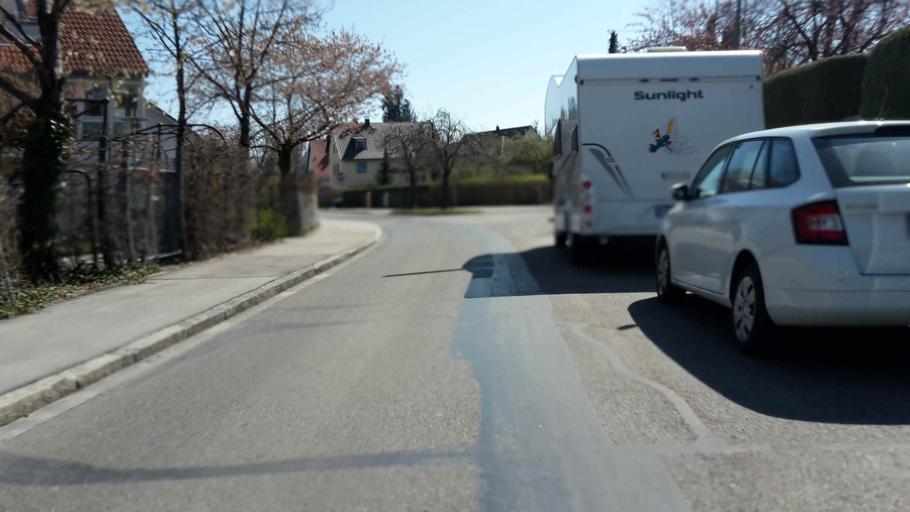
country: DE
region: Bavaria
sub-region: Upper Bavaria
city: Karlsfeld
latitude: 48.1799
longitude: 11.4737
